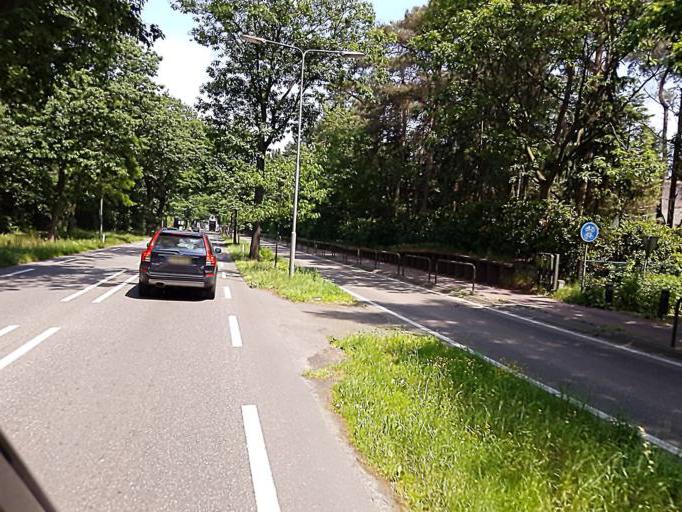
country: NL
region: North Brabant
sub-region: Gemeente Waalre
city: Waalre
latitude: 51.3893
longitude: 5.4739
